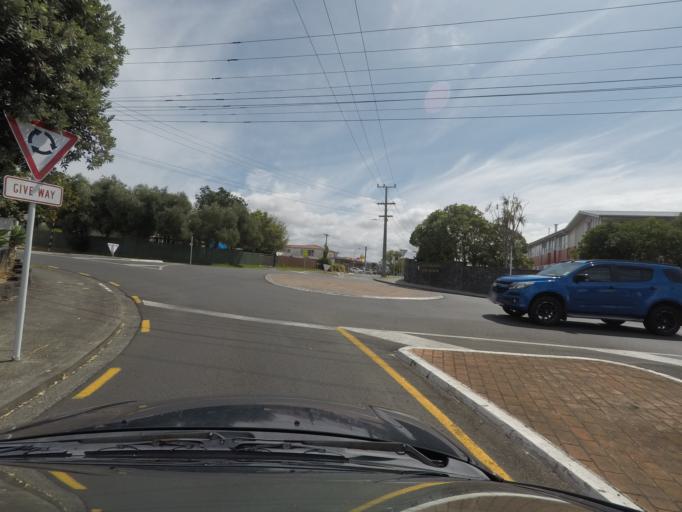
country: NZ
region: Auckland
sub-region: Auckland
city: Waitakere
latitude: -36.9006
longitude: 174.6666
